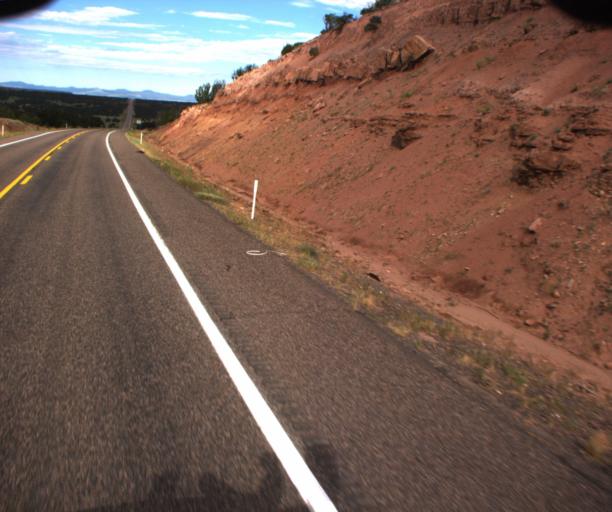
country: US
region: Arizona
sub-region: Apache County
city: Springerville
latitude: 34.1640
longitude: -109.0592
